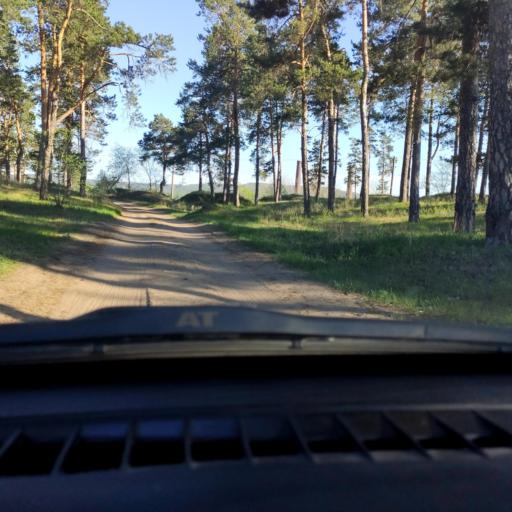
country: RU
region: Samara
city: Zhigulevsk
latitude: 53.4683
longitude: 49.5613
